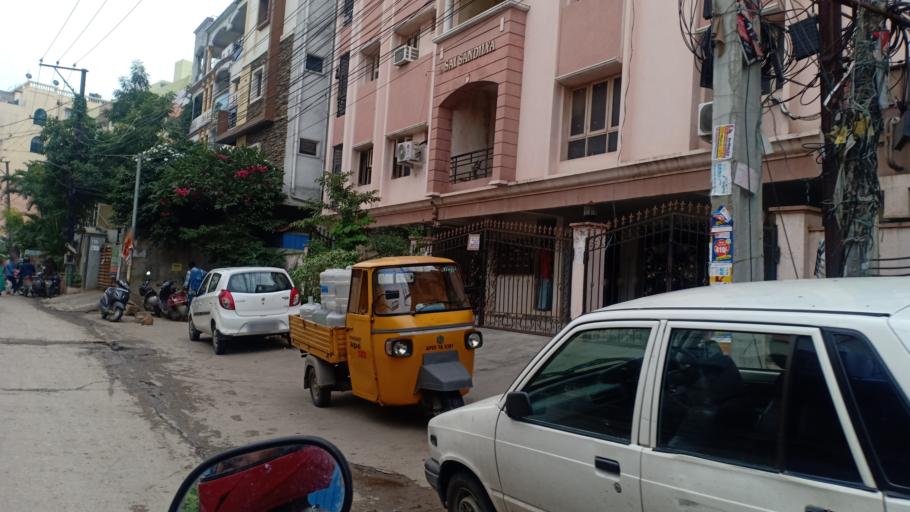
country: IN
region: Telangana
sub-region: Hyderabad
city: Hyderabad
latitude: 17.4328
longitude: 78.4404
